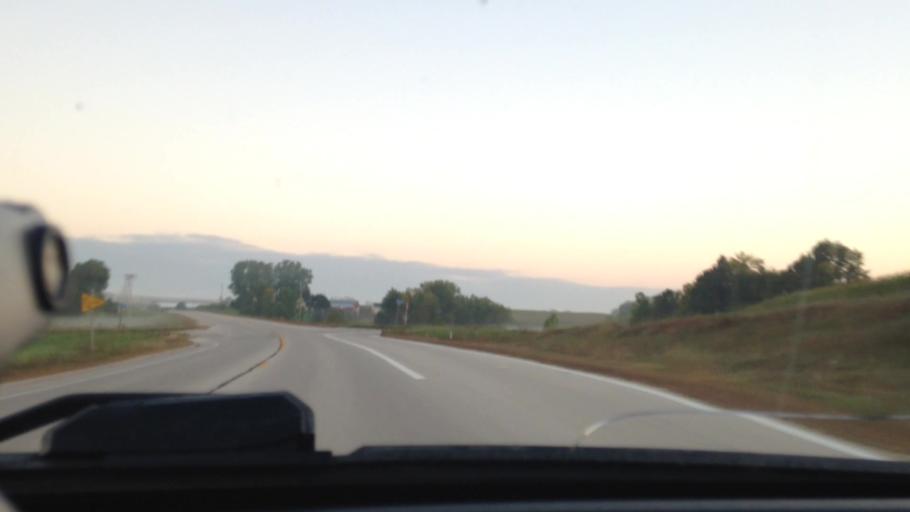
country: US
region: Wisconsin
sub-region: Dodge County
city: Lomira
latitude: 43.5648
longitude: -88.4470
